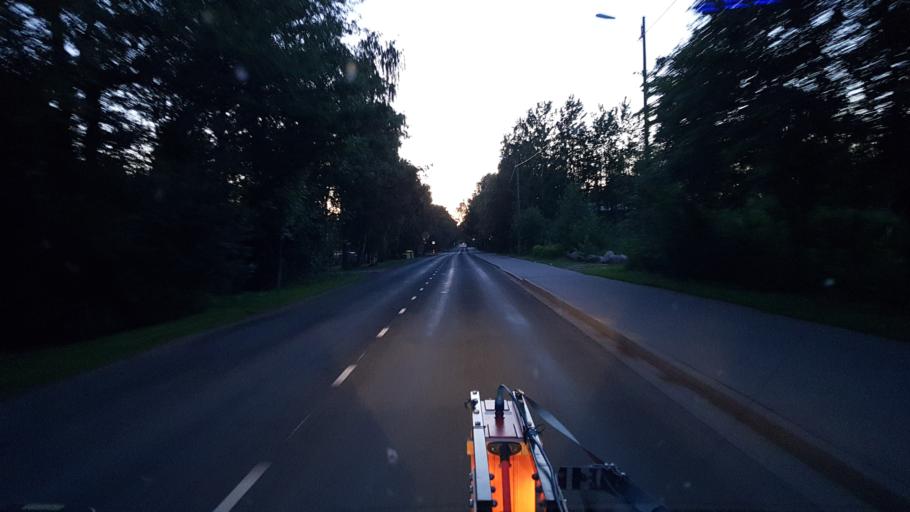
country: EE
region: Harju
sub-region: Harku vald
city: Tabasalu
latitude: 59.4381
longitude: 24.5989
